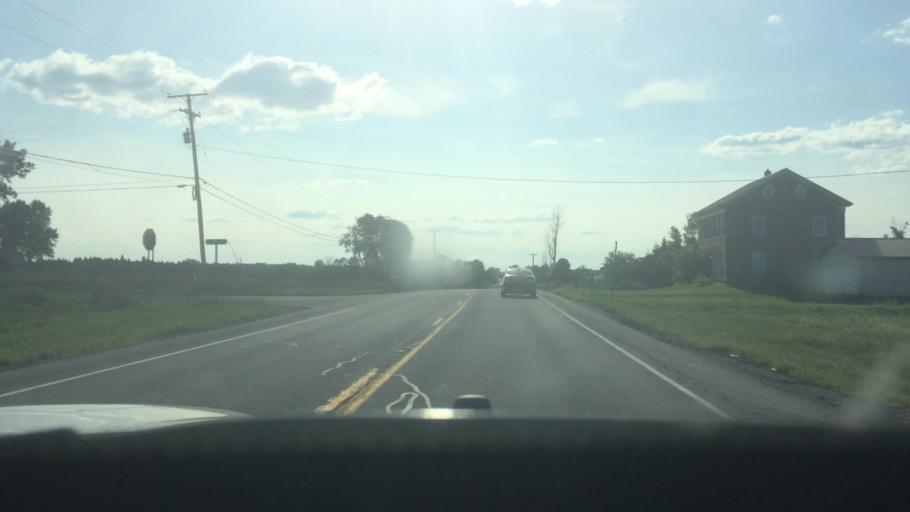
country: US
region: New York
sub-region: St. Lawrence County
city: Potsdam
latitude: 44.6882
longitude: -74.7646
